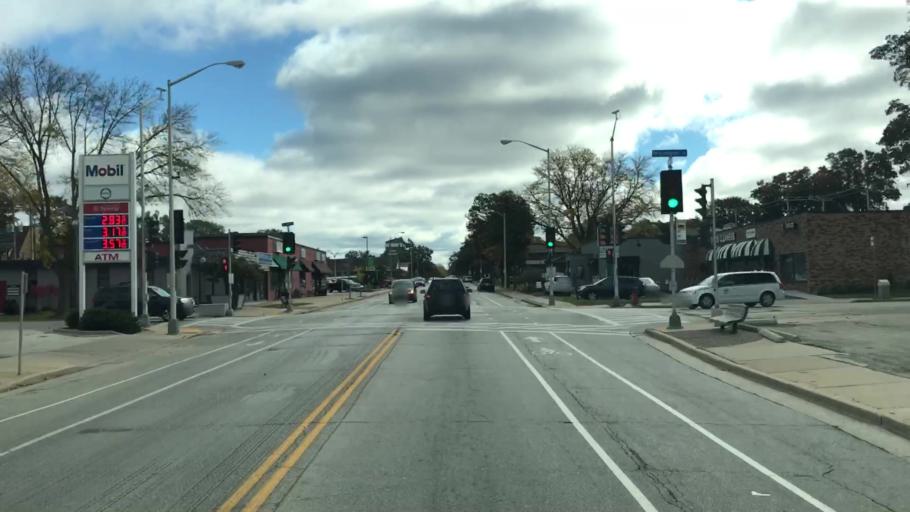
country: US
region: Wisconsin
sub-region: Milwaukee County
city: Wauwatosa
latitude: 43.0605
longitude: -88.0230
